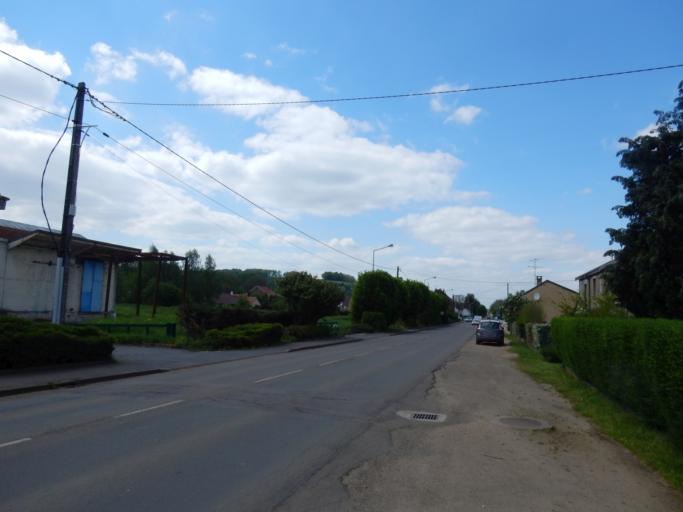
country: FR
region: Champagne-Ardenne
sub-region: Departement des Ardennes
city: Bazeilles
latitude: 49.6568
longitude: 4.9862
